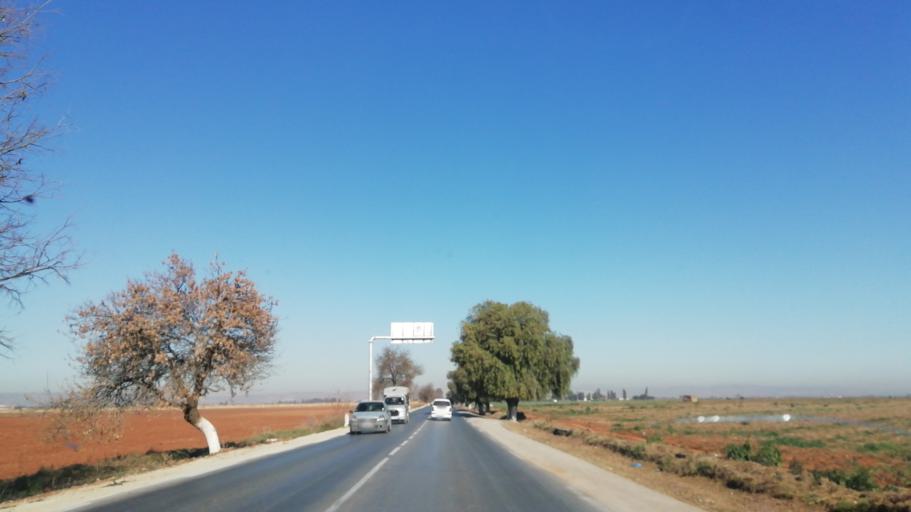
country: DZ
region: Mascara
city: Mascara
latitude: 35.2768
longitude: 0.1284
